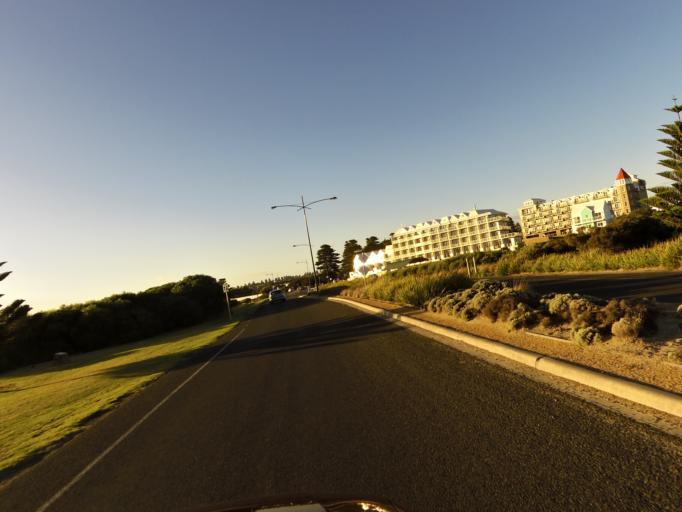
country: AU
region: Victoria
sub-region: Warrnambool
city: Warrnambool
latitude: -38.3987
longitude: 142.4721
